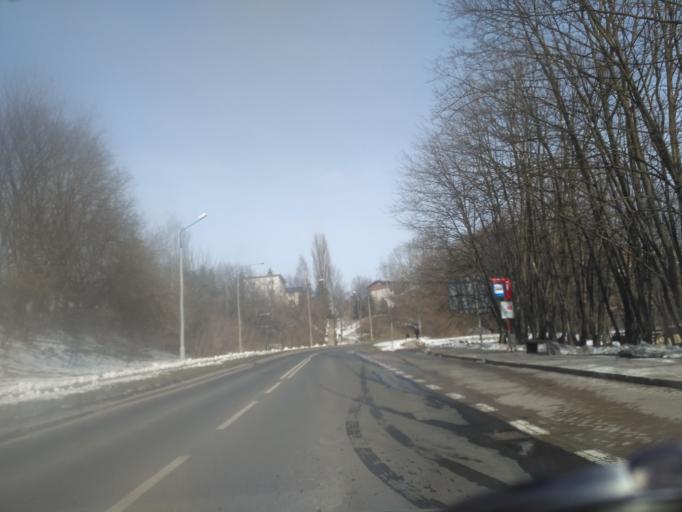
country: PL
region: Lublin Voivodeship
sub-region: Powiat lubelski
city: Lublin
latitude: 51.2592
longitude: 22.5383
